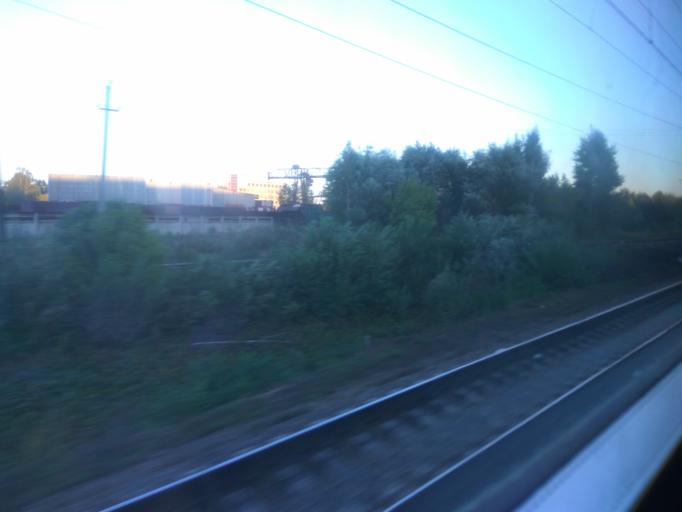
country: RU
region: Moskovskaya
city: Elektrostal'
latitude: 55.7741
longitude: 38.4664
